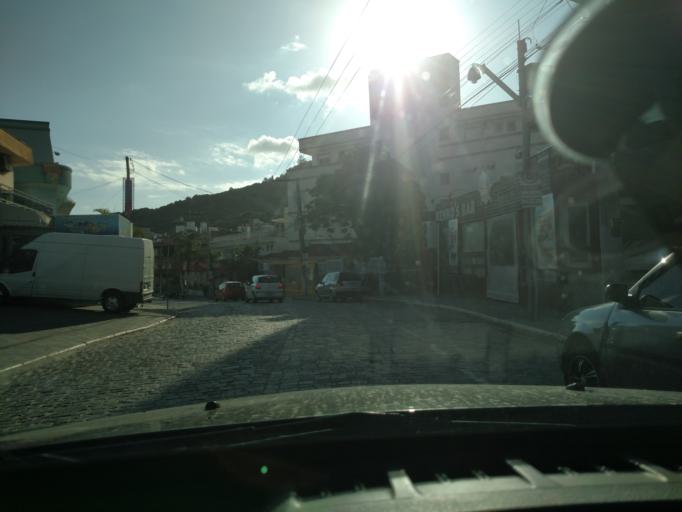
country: BR
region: Santa Catarina
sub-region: Porto Belo
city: Porto Belo
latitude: -27.1494
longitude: -48.4851
